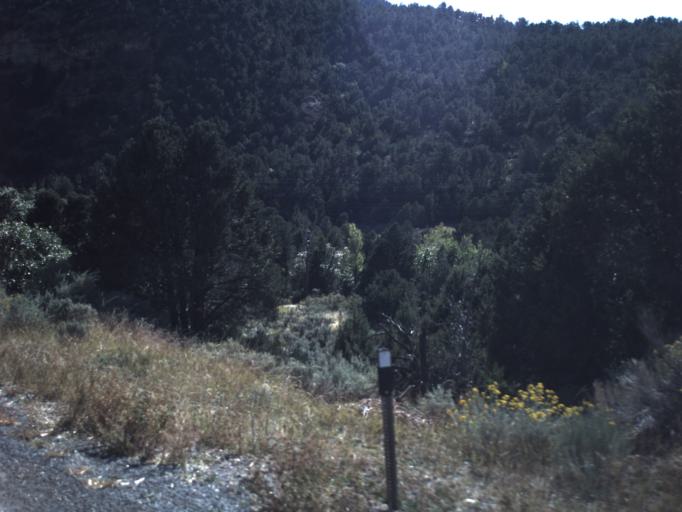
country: US
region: Utah
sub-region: Iron County
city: Parowan
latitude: 37.8233
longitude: -112.8114
